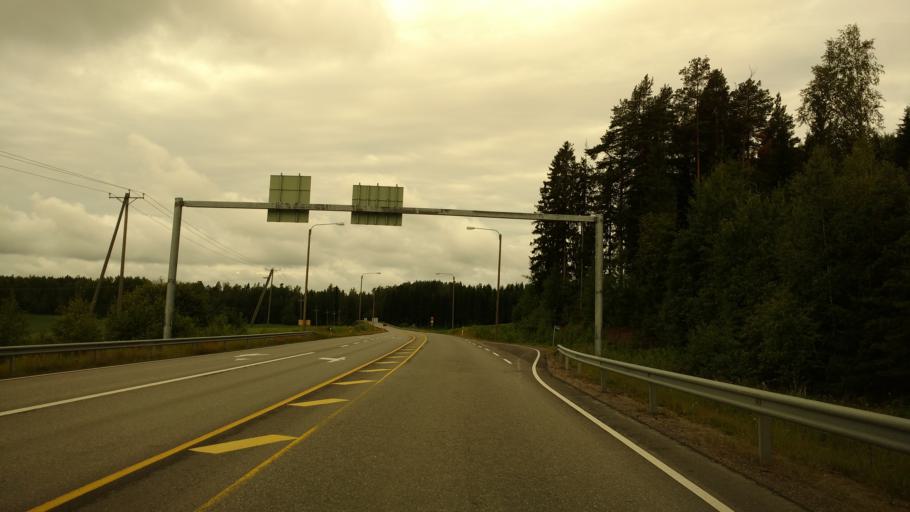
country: FI
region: Varsinais-Suomi
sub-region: Salo
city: Salo
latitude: 60.4382
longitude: 23.1831
